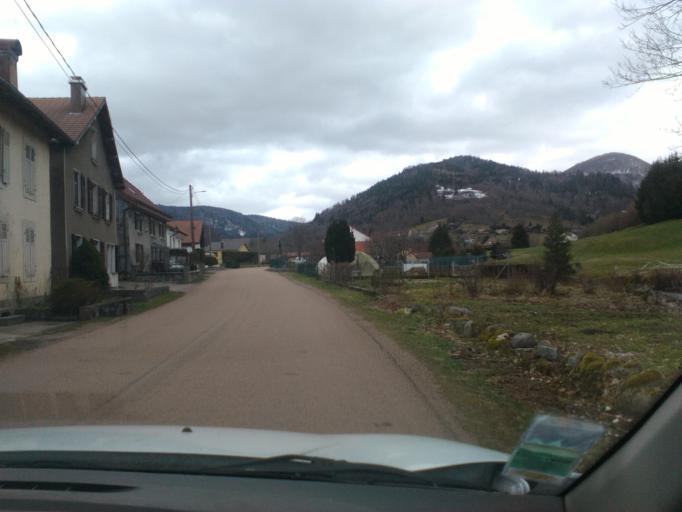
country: FR
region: Lorraine
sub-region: Departement des Vosges
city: Bussang
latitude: 47.8894
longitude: 6.8629
